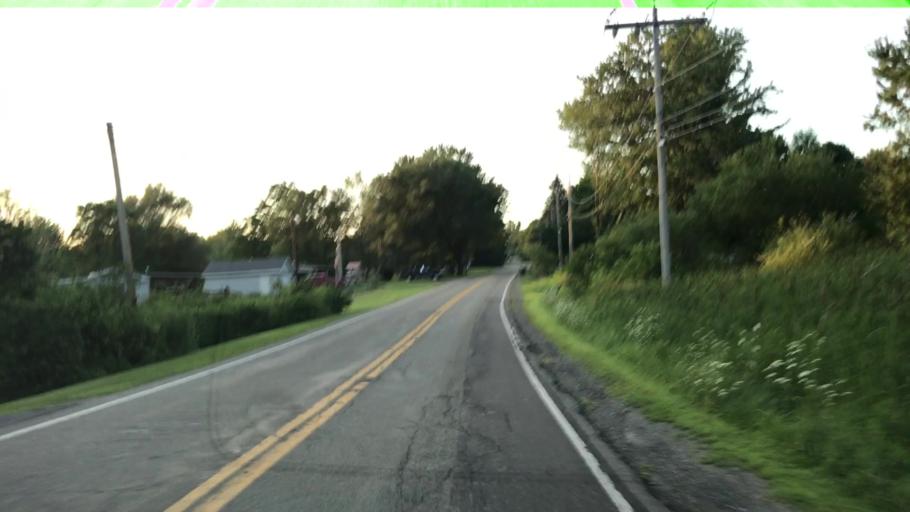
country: US
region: New York
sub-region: Chautauqua County
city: Mayville
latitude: 42.2626
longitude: -79.4704
